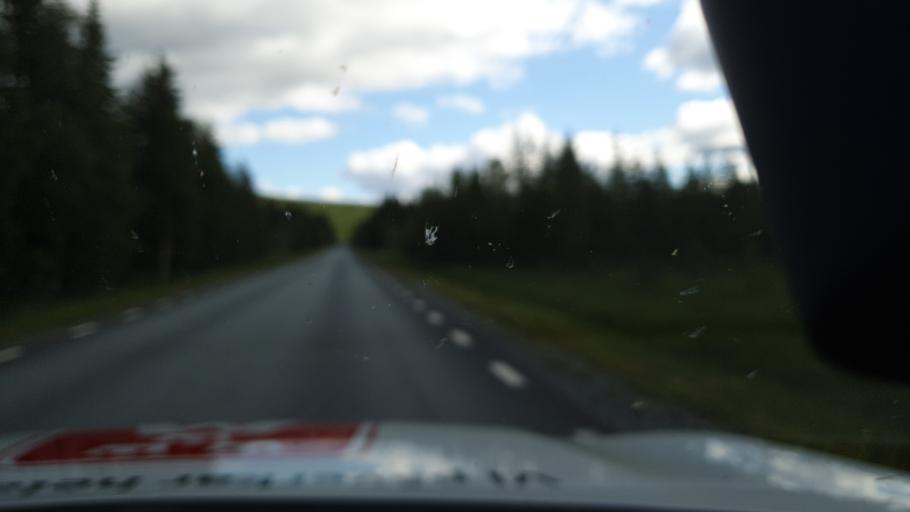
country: SE
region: Vaesterbotten
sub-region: Mala Kommun
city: Mala
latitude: 65.1504
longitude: 18.6732
